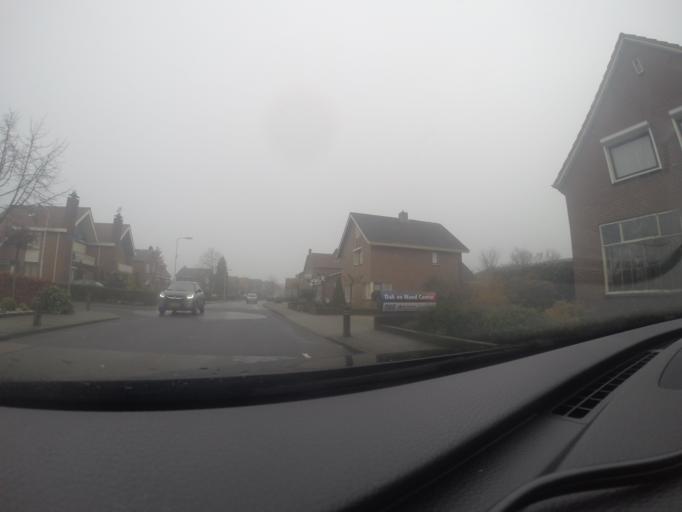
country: NL
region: Gelderland
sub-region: Oost Gelre
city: Lichtenvoorde
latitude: 52.0026
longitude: 6.5203
